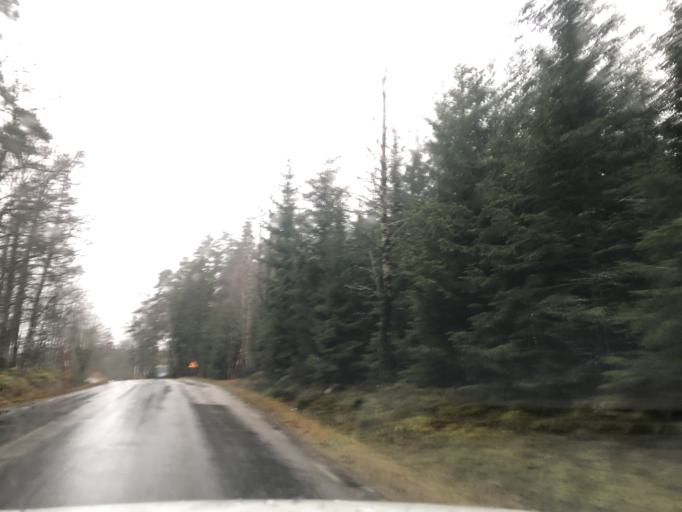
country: SE
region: Vaestra Goetaland
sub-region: Ulricehamns Kommun
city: Ulricehamn
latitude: 57.8369
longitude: 13.5334
